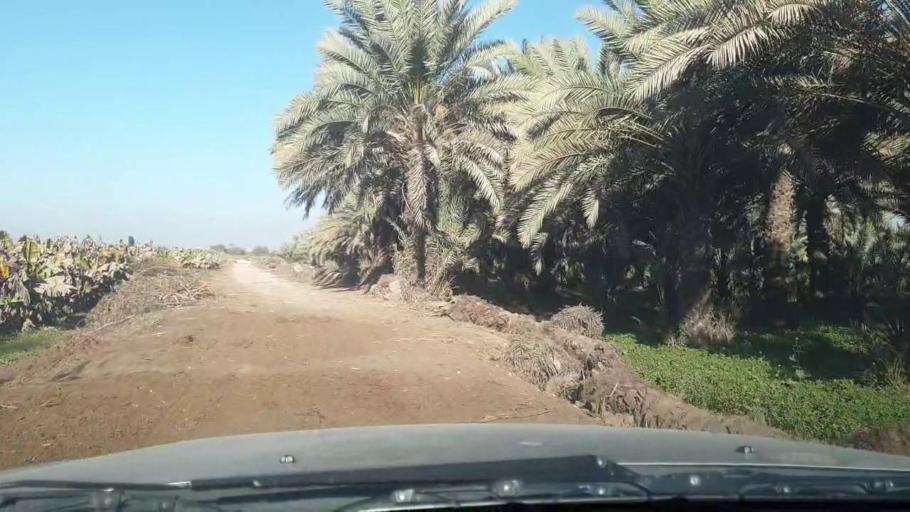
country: PK
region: Sindh
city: Adilpur
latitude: 27.9505
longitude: 69.1969
